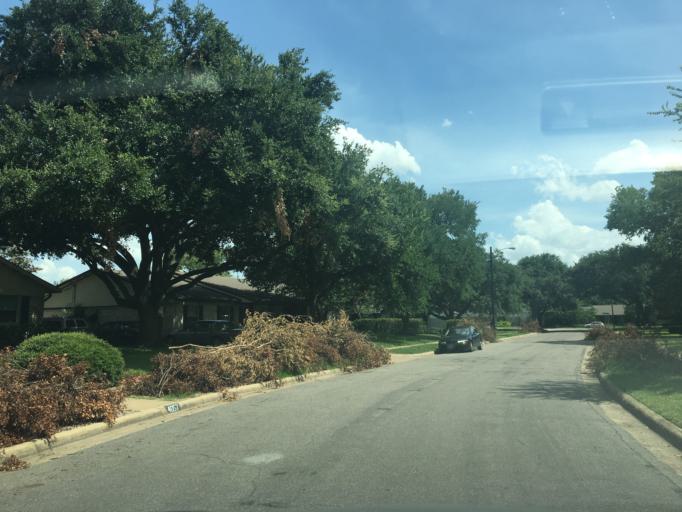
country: US
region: Texas
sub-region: Dallas County
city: Addison
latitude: 32.9139
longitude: -96.8451
